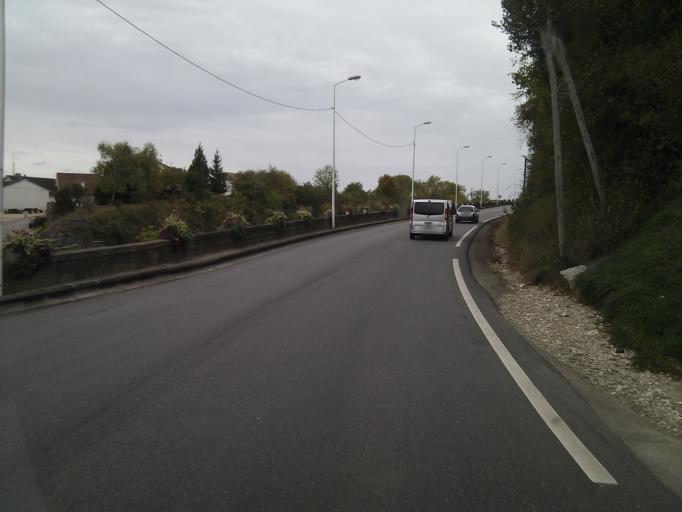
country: FR
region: Lorraine
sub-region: Departement des Vosges
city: Neufchateau
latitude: 48.3635
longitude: 5.6930
